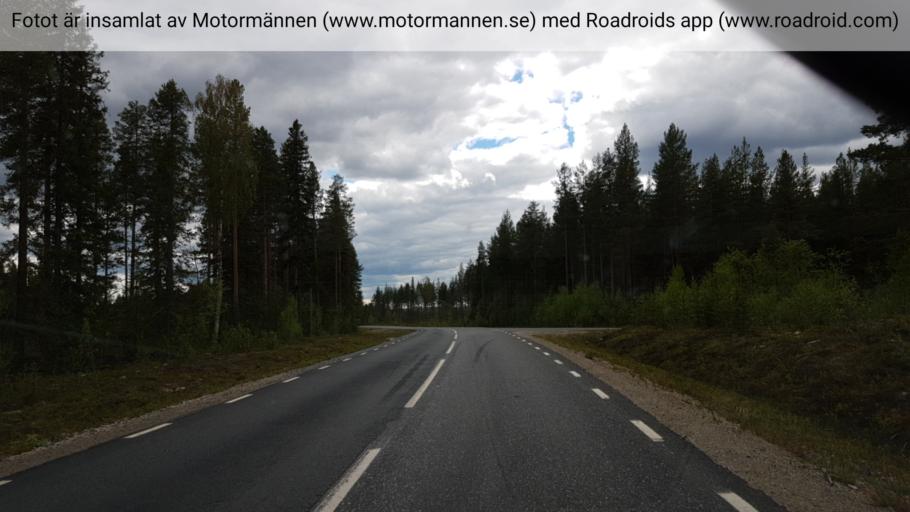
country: SE
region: Vaesterbotten
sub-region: Vindelns Kommun
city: Vindeln
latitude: 64.5556
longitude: 19.9202
